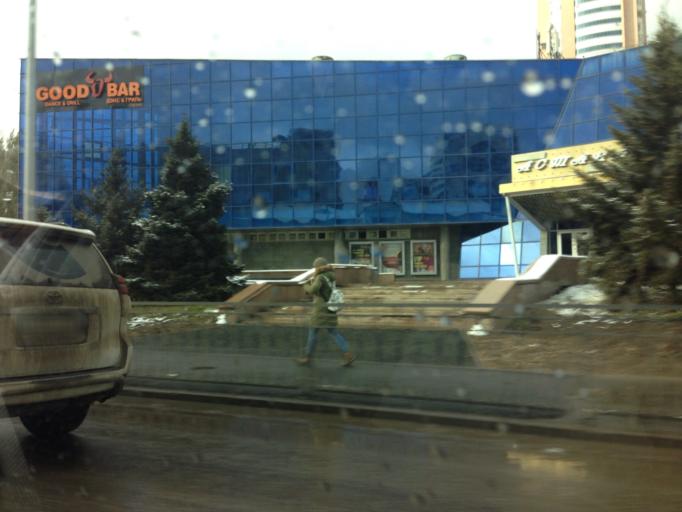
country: KZ
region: Astana Qalasy
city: Astana
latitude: 51.1633
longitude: 71.4315
